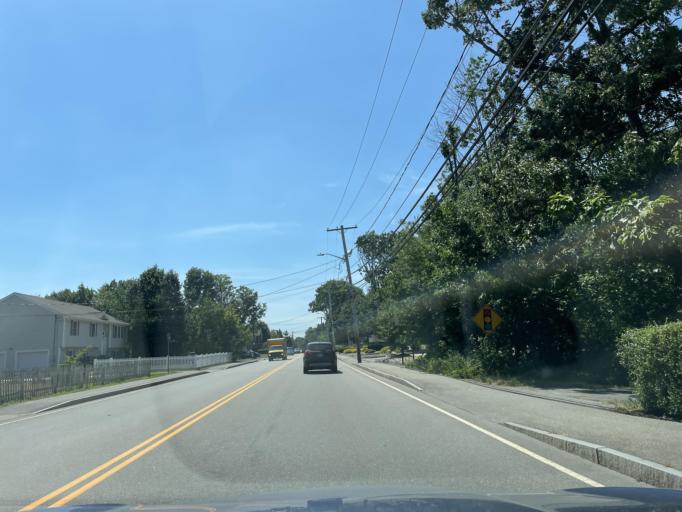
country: US
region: Massachusetts
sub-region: Norfolk County
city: Stoughton
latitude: 42.1345
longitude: -71.1069
